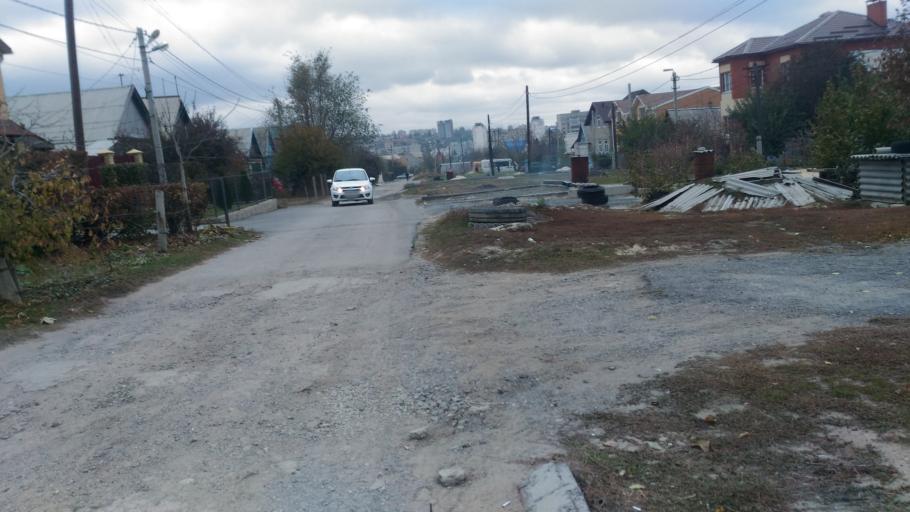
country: RU
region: Volgograd
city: Volgograd
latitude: 48.6465
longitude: 44.4275
